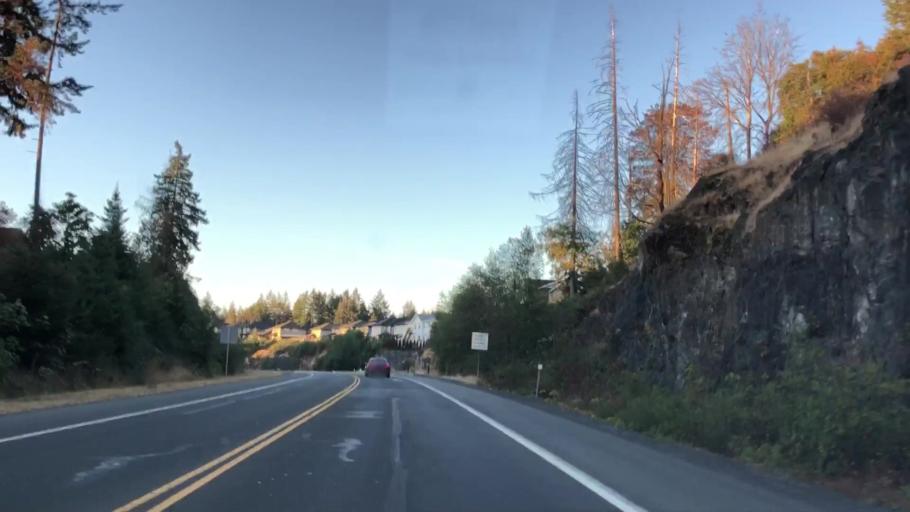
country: CA
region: British Columbia
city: Colwood
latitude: 48.4196
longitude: -123.5053
